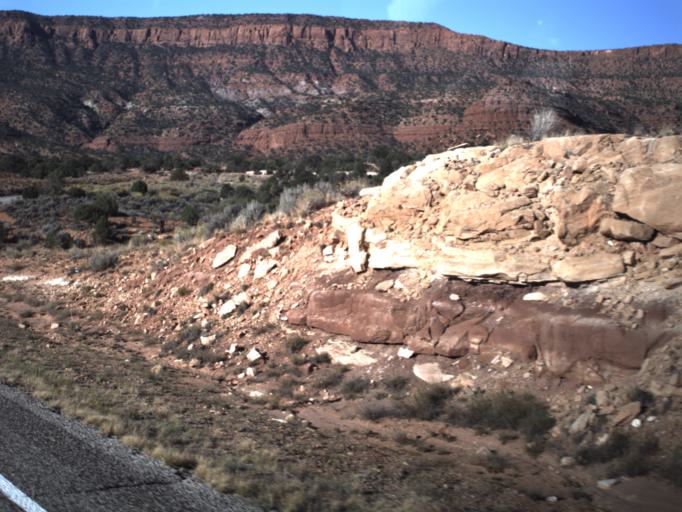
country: US
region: Utah
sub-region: San Juan County
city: Blanding
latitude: 37.6372
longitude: -110.1490
